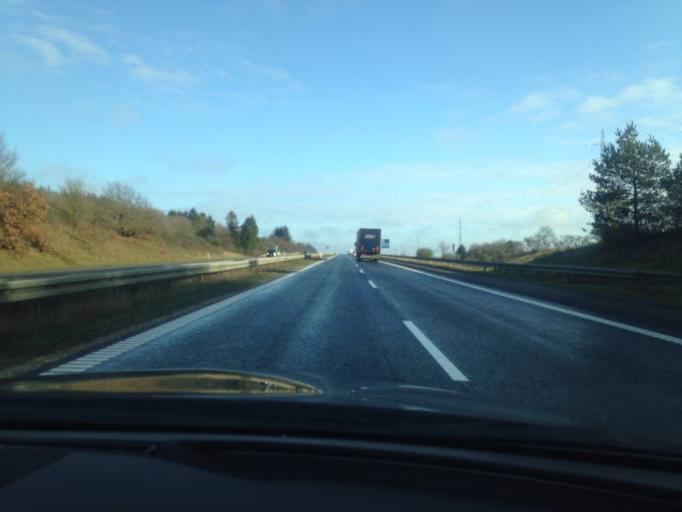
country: DK
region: South Denmark
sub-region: Kolding Kommune
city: Lunderskov
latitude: 55.5102
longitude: 9.3735
